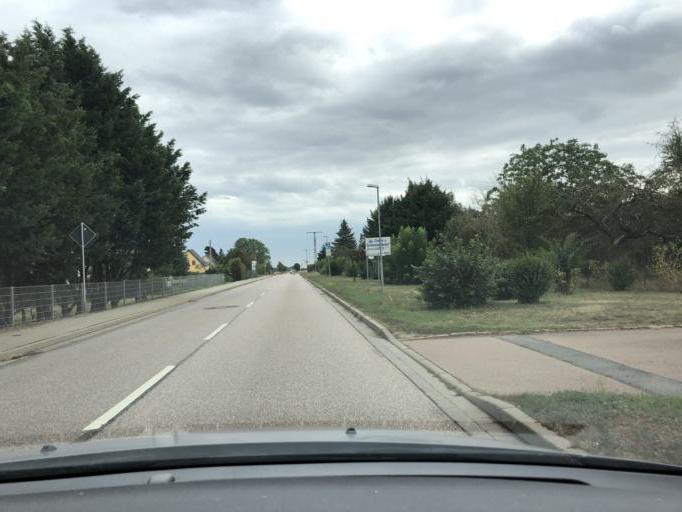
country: DE
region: Saxony-Anhalt
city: Wulfen
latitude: 51.7716
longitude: 11.9122
